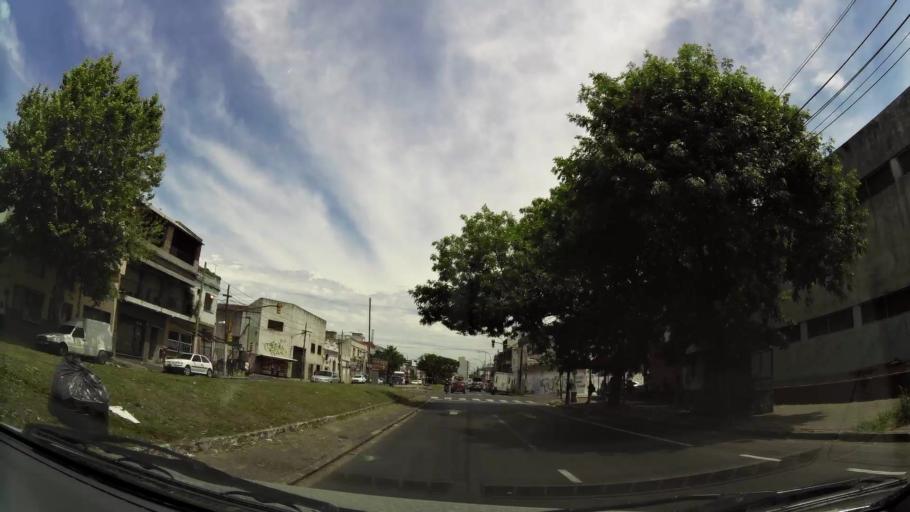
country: AR
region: Buenos Aires
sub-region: Partido de Lanus
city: Lanus
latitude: -34.6736
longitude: -58.3962
